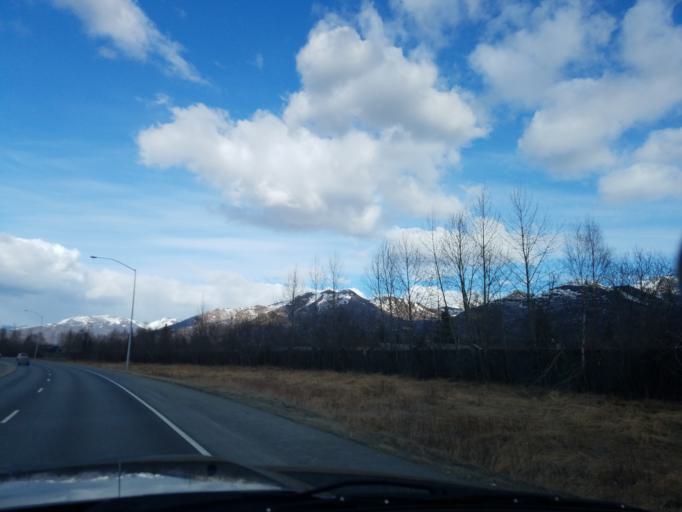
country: US
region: Alaska
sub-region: Anchorage Municipality
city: Elmendorf Air Force Base
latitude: 61.1819
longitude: -149.7383
